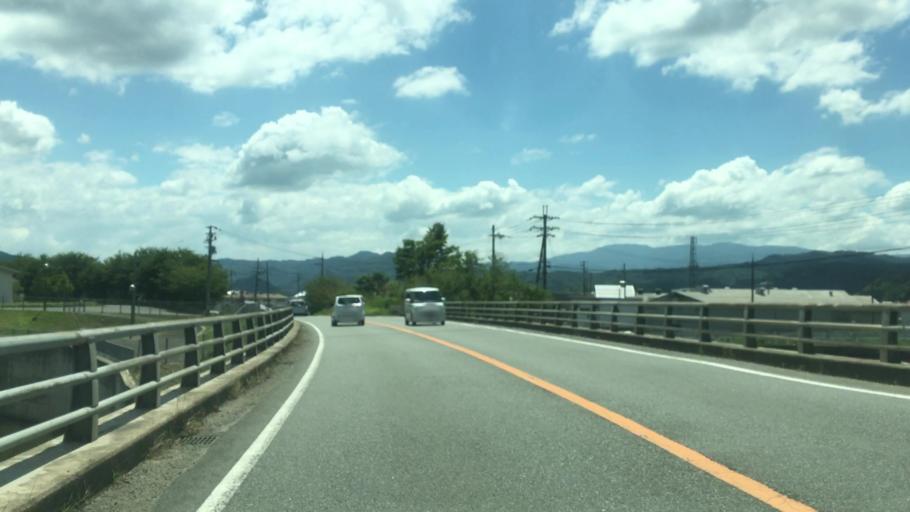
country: JP
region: Hyogo
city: Toyooka
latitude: 35.5006
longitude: 134.8067
